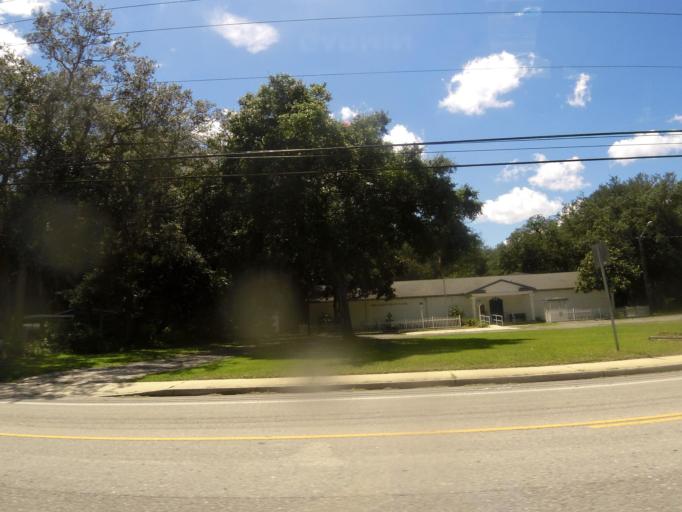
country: US
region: Florida
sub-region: Nassau County
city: Fernandina Beach
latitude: 30.6560
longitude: -81.4536
